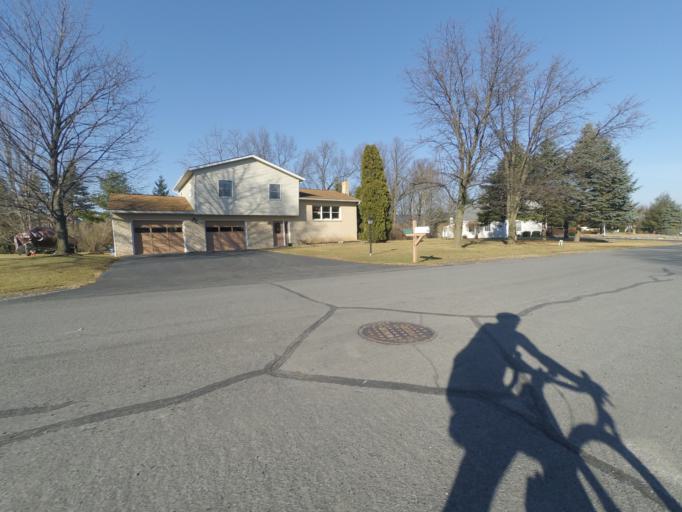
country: US
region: Pennsylvania
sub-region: Centre County
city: Boalsburg
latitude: 40.7764
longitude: -77.8061
